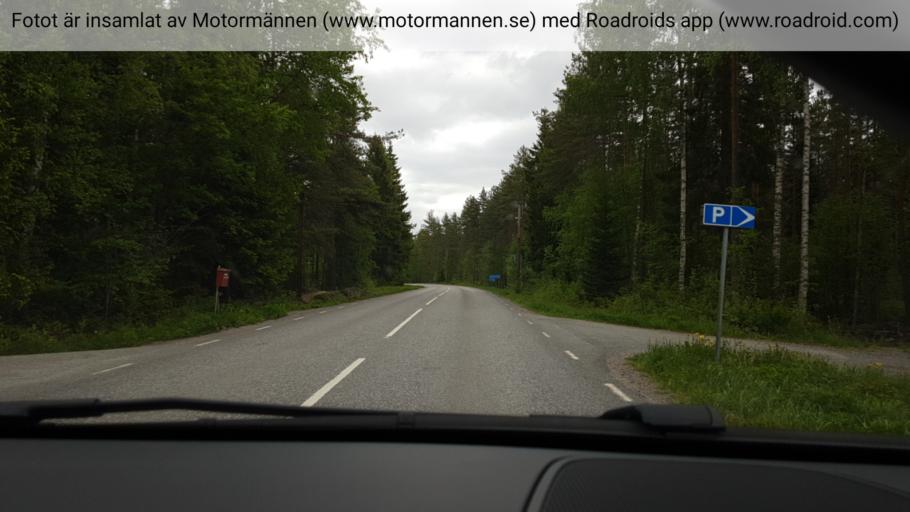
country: SE
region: Uppsala
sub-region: Heby Kommun
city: OEstervala
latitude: 60.0950
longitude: 17.1570
